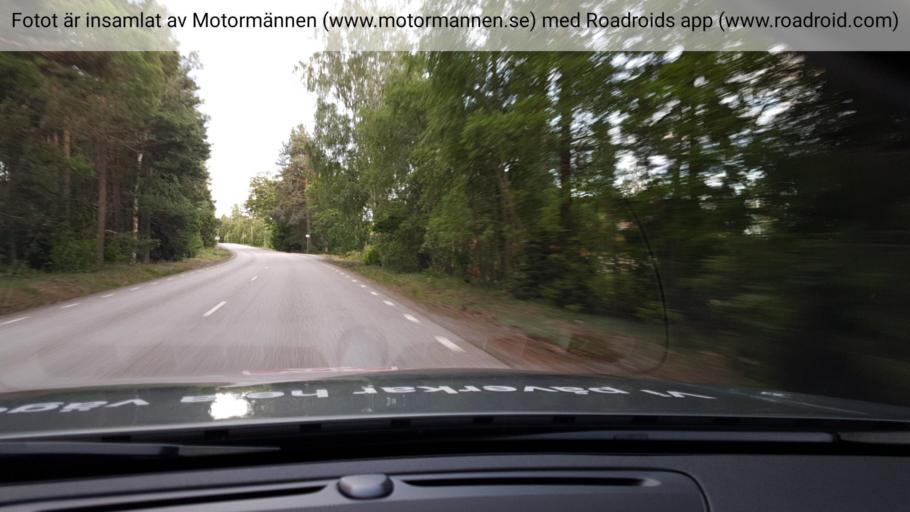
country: SE
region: Vaestmanland
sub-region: Sala Kommun
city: Sala
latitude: 59.8338
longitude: 16.5061
